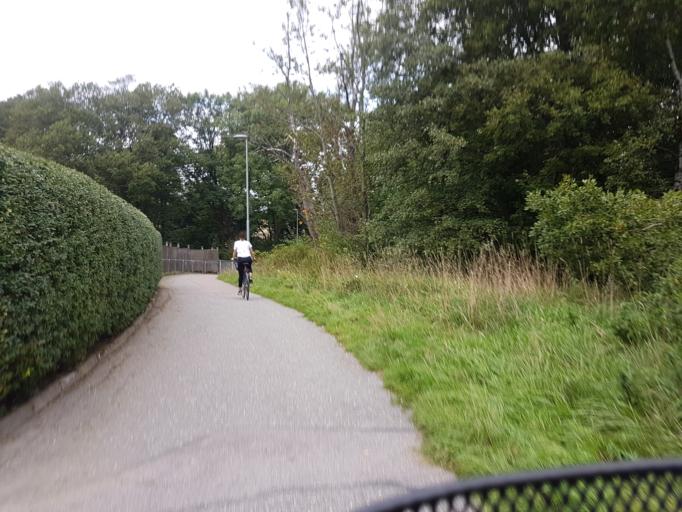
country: SE
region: Vaestra Goetaland
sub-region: Ale Kommun
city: Nodinge-Nol
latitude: 57.8907
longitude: 12.0490
